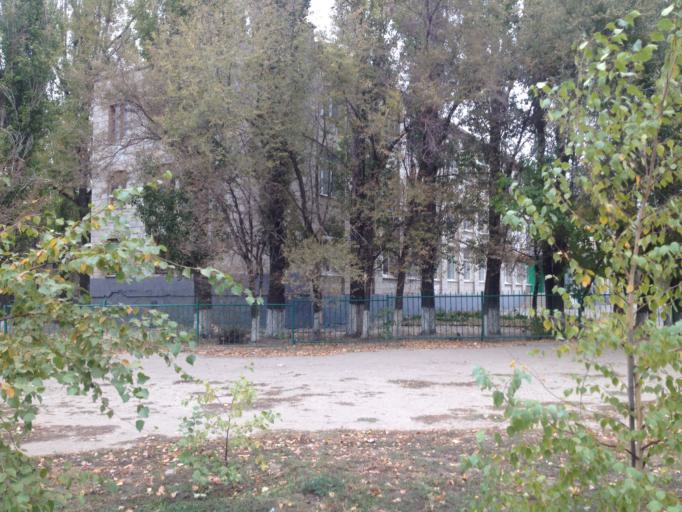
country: RU
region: Volgograd
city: Volgograd
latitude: 48.7375
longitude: 44.4878
